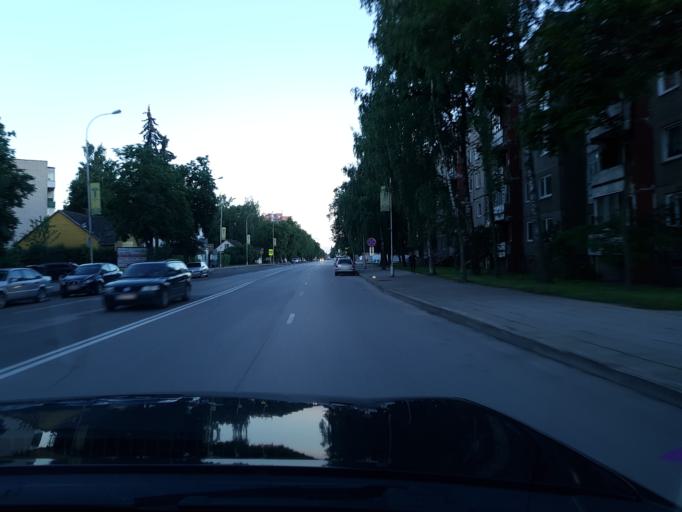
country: LT
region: Marijampoles apskritis
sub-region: Marijampole Municipality
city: Marijampole
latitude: 54.5675
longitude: 23.3598
